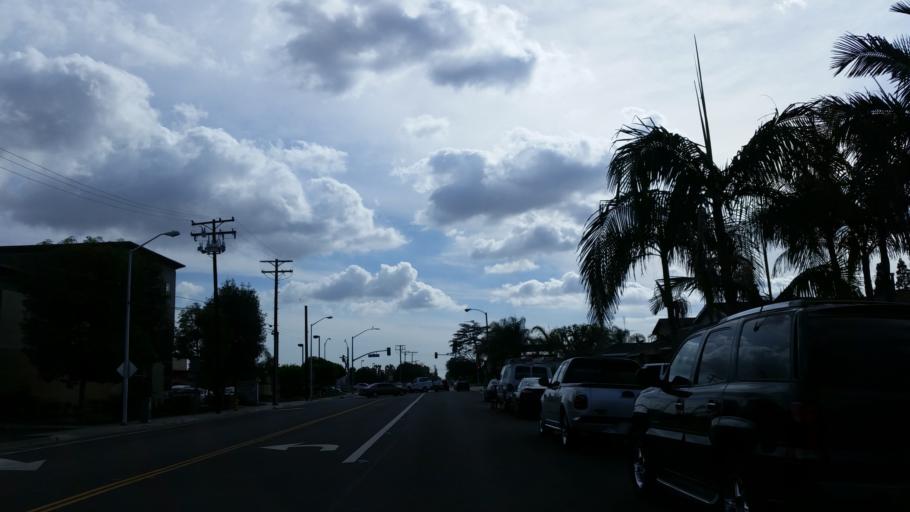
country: US
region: California
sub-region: Los Angeles County
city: Downey
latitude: 33.9184
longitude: -118.1342
